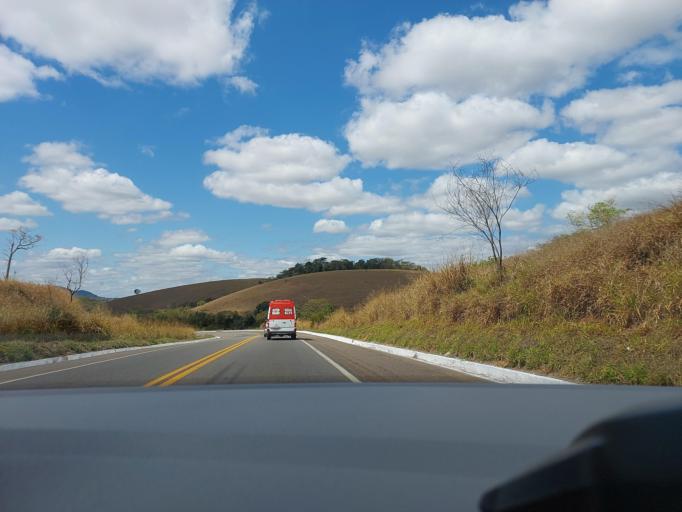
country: BR
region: Minas Gerais
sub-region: Muriae
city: Muriae
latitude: -21.1383
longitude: -42.3086
